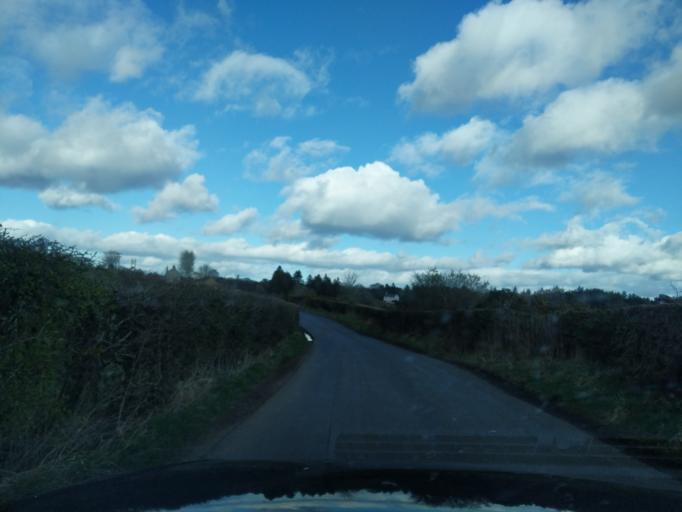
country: GB
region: Scotland
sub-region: Edinburgh
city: Balerno
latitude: 55.8769
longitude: -3.3796
